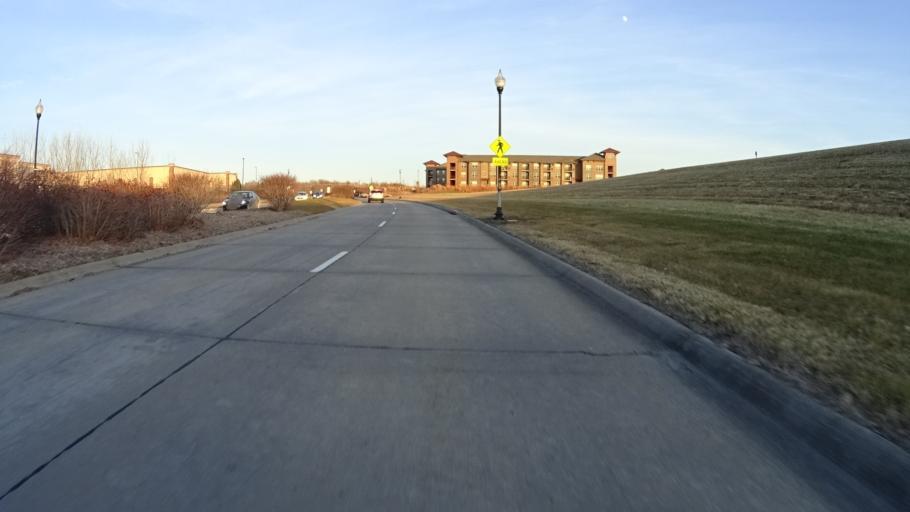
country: US
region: Nebraska
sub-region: Sarpy County
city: Papillion
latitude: 41.1318
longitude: -96.0288
